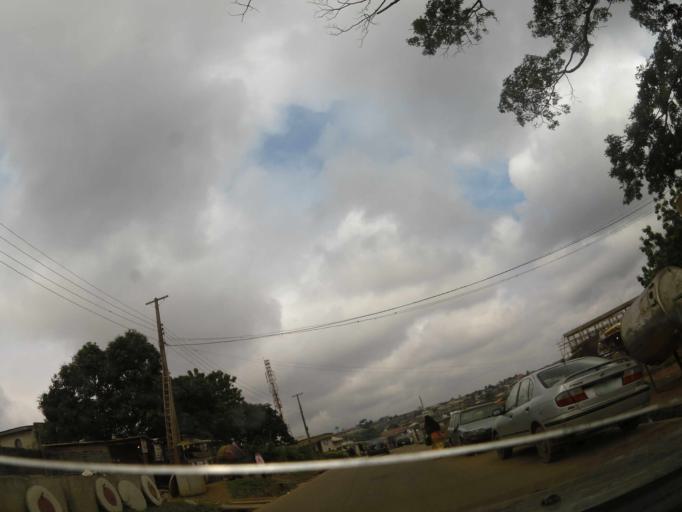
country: NG
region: Oyo
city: Ibadan
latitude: 7.4366
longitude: 3.9481
